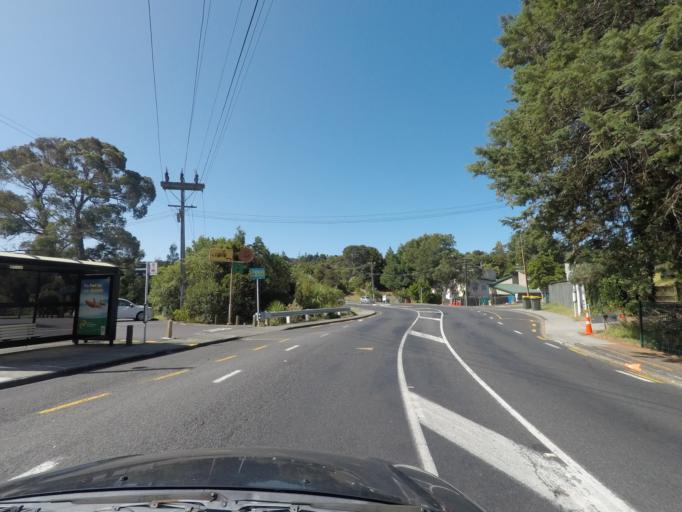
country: NZ
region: Auckland
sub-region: Auckland
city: Waitakere
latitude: -36.9243
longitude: 174.6556
